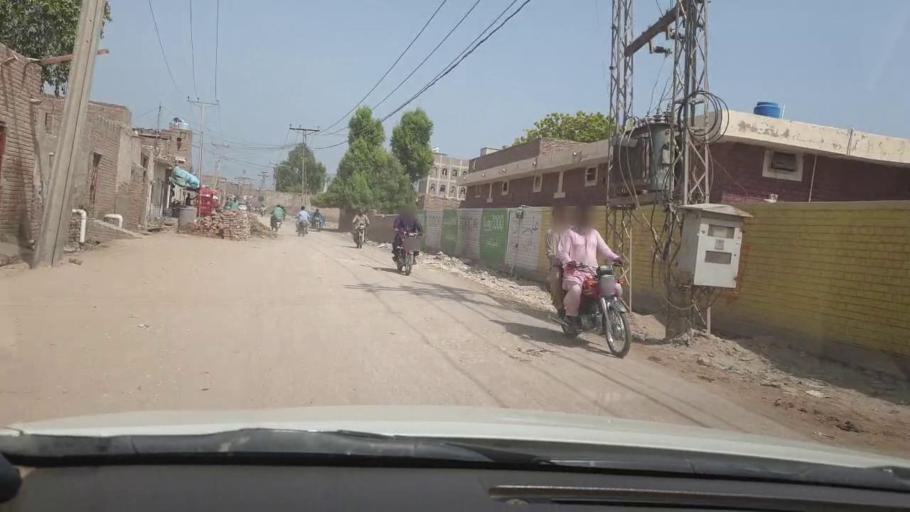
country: PK
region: Sindh
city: Shikarpur
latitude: 27.9531
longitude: 68.6256
